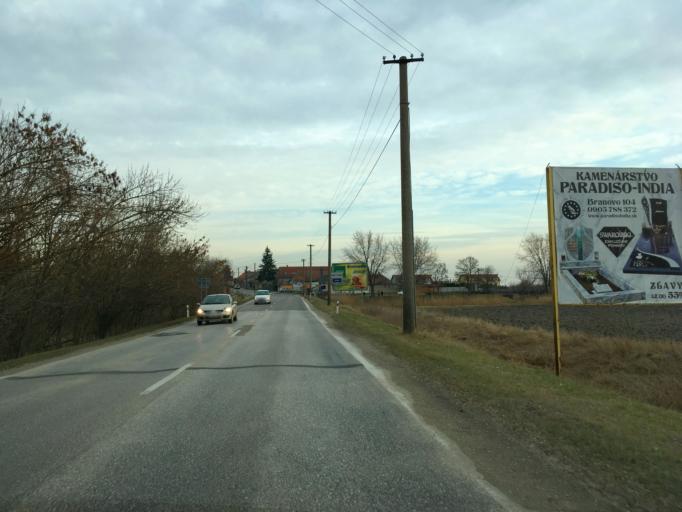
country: SK
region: Nitriansky
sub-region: Okres Nove Zamky
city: Nove Zamky
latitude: 47.9960
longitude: 18.2573
